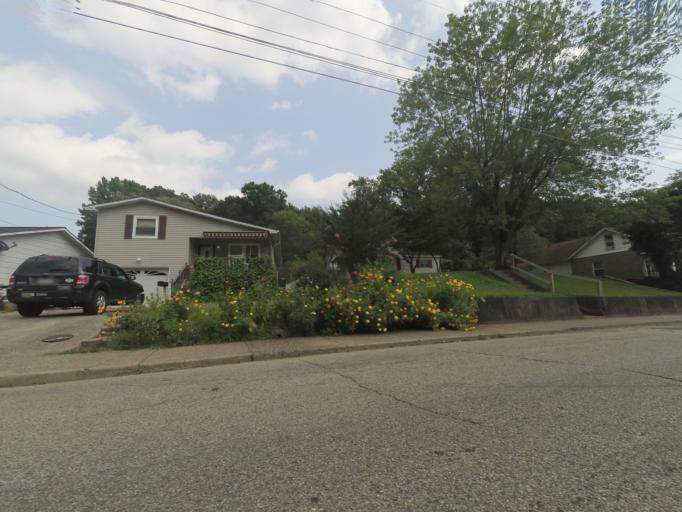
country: US
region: West Virginia
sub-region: Cabell County
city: Huntington
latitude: 38.4131
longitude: -82.4013
